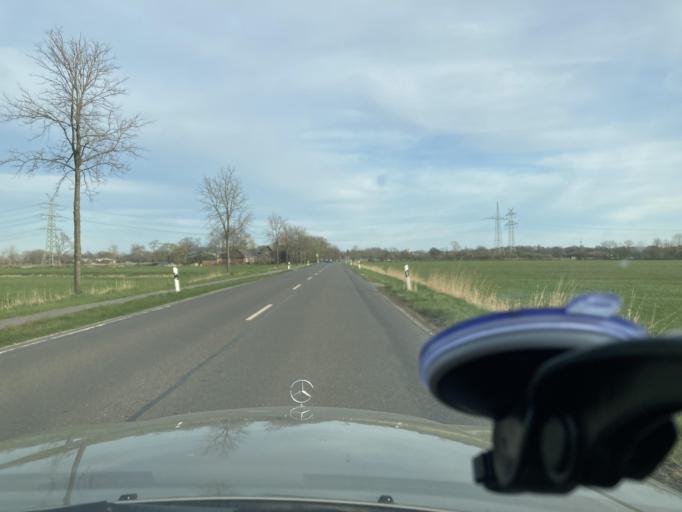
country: DE
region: Schleswig-Holstein
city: Stelle-Wittenwurth
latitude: 54.2466
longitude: 9.0726
